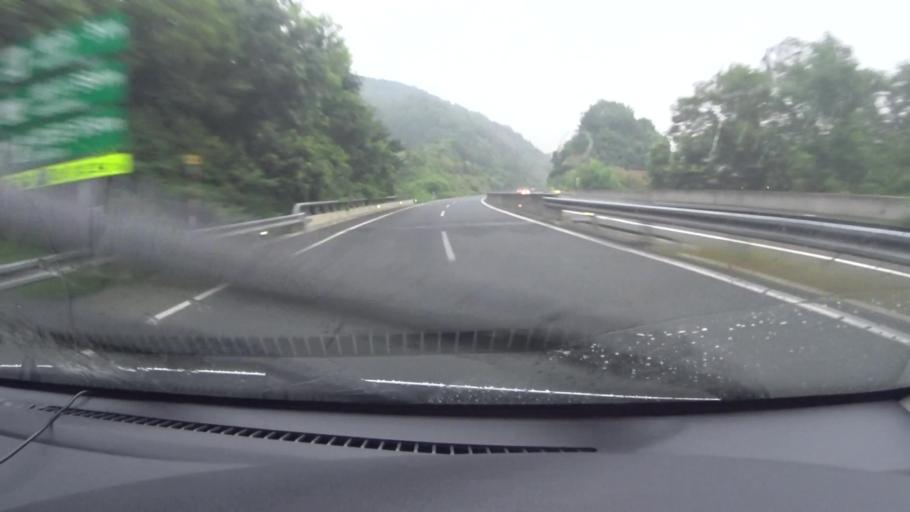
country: JP
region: Kyoto
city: Kameoka
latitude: 35.1015
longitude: 135.4926
